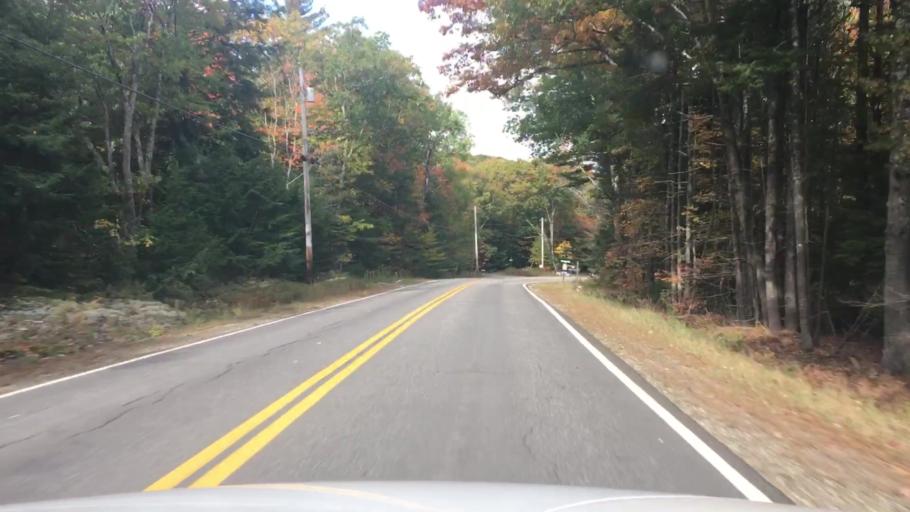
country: US
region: Maine
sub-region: Knox County
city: Hope
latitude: 44.2498
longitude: -69.1275
